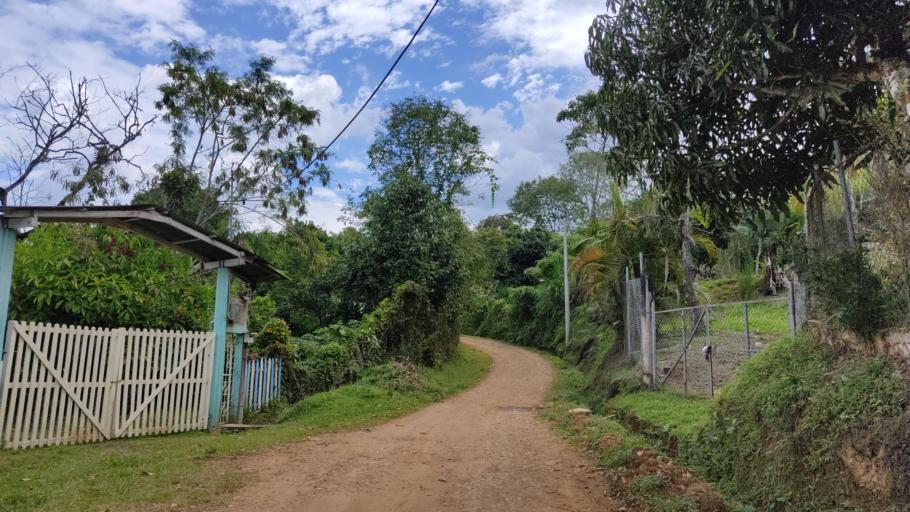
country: CO
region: Valle del Cauca
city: Jamundi
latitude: 3.2092
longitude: -76.6566
